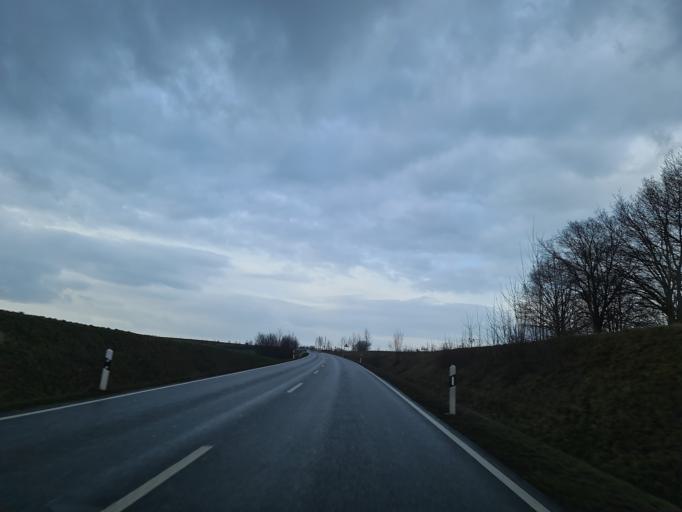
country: DE
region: Saxony
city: Reinsdorf
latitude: 50.6909
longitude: 12.5957
